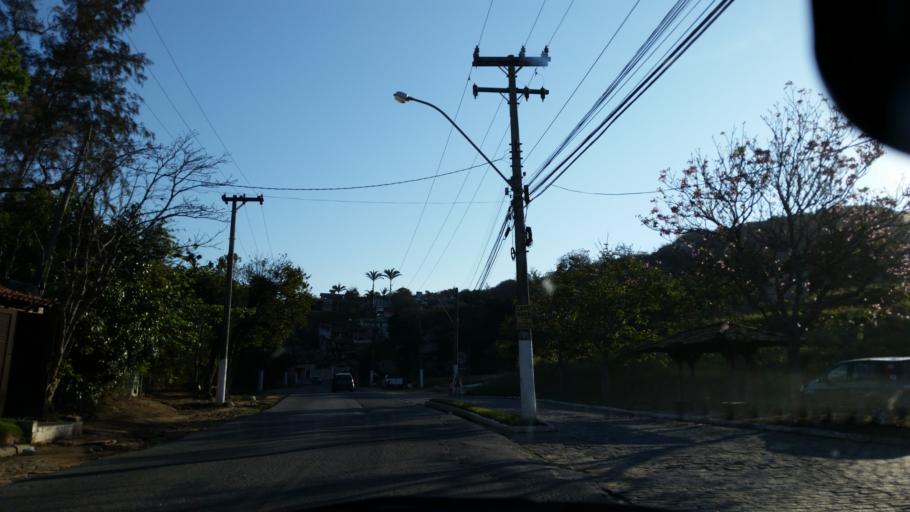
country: BR
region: Rio de Janeiro
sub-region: Armacao De Buzios
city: Armacao de Buzios
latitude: -22.7637
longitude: -41.8979
